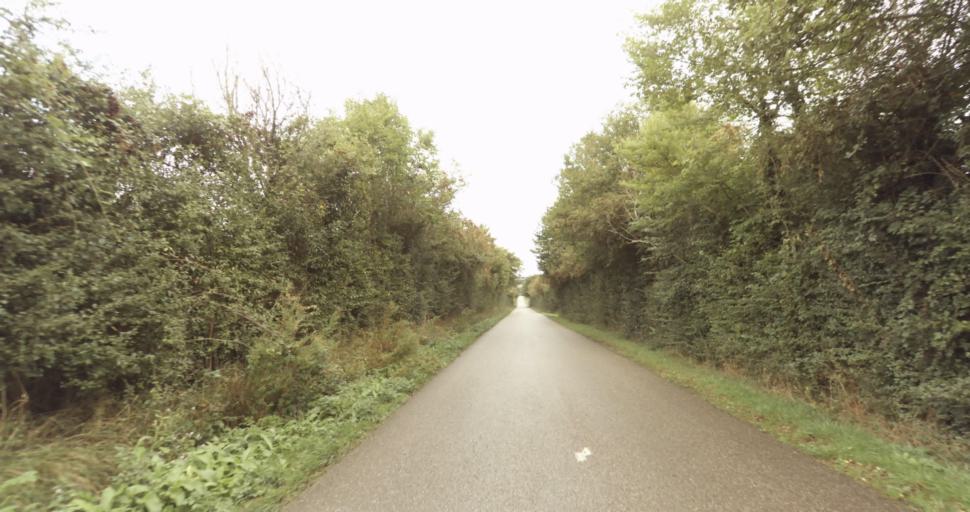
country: FR
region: Lower Normandy
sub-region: Departement de l'Orne
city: Vimoutiers
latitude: 48.8661
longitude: 0.2238
